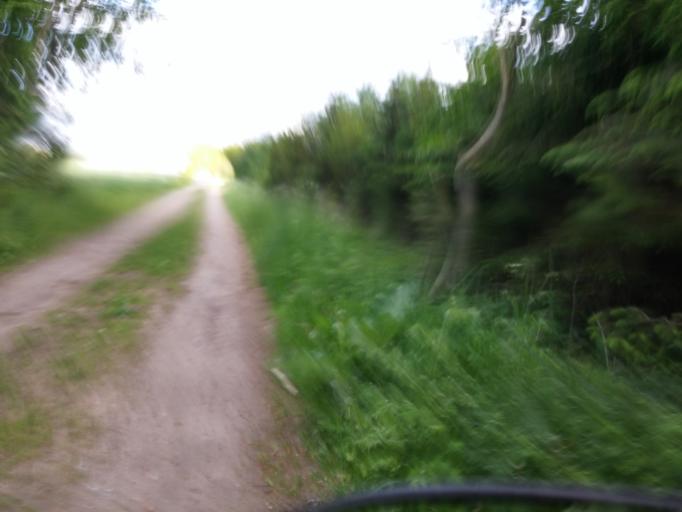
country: DK
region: South Denmark
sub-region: Kerteminde Kommune
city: Munkebo
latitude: 55.4248
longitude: 10.5540
